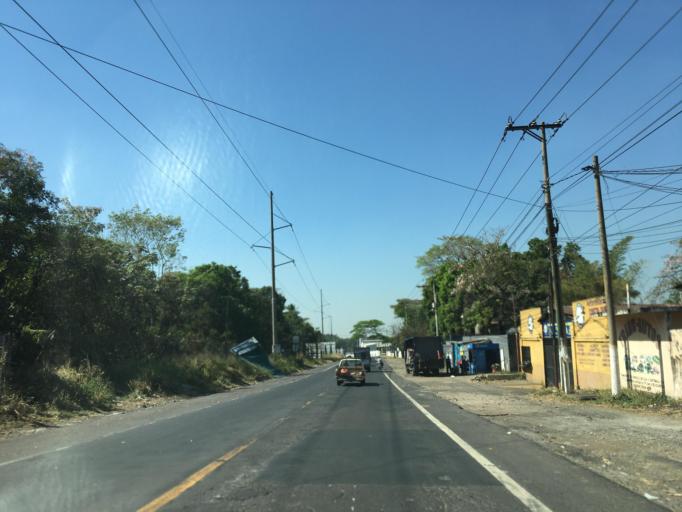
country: GT
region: Escuintla
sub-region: Municipio de Escuintla
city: Escuintla
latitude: 14.2807
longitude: -90.7884
